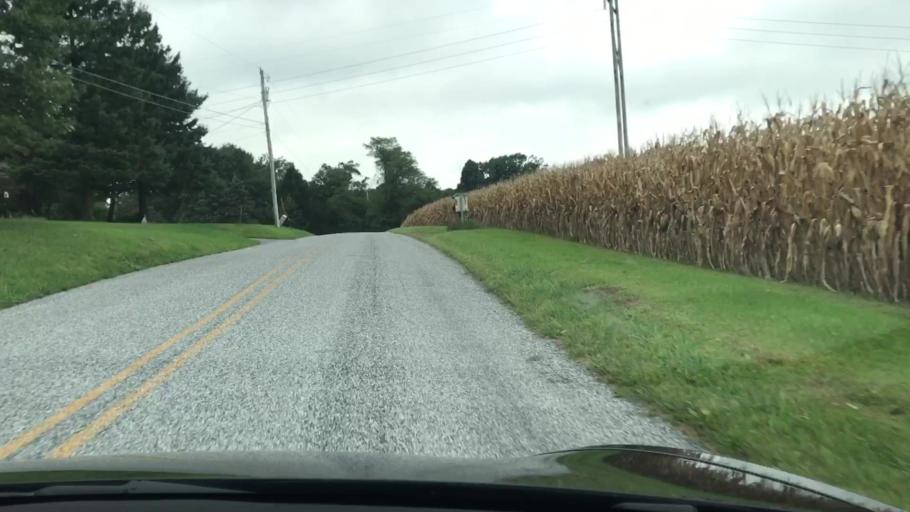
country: US
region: Pennsylvania
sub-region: York County
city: Dillsburg
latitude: 40.1128
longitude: -76.9605
